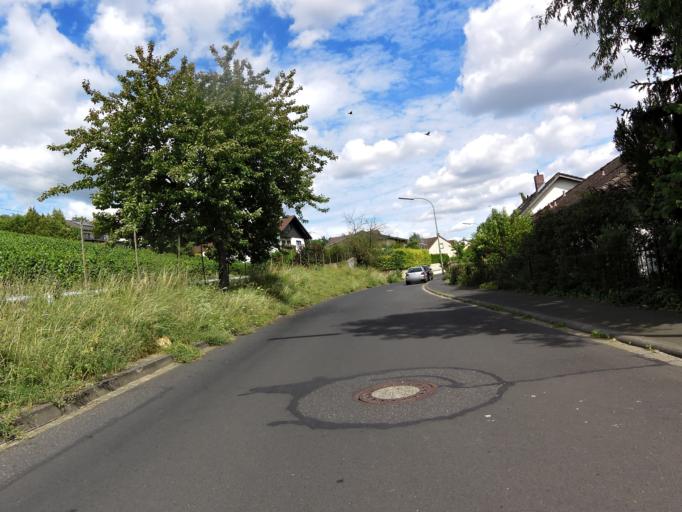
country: DE
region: Bavaria
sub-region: Regierungsbezirk Unterfranken
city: Zell am Main
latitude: 49.8161
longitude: 9.8845
